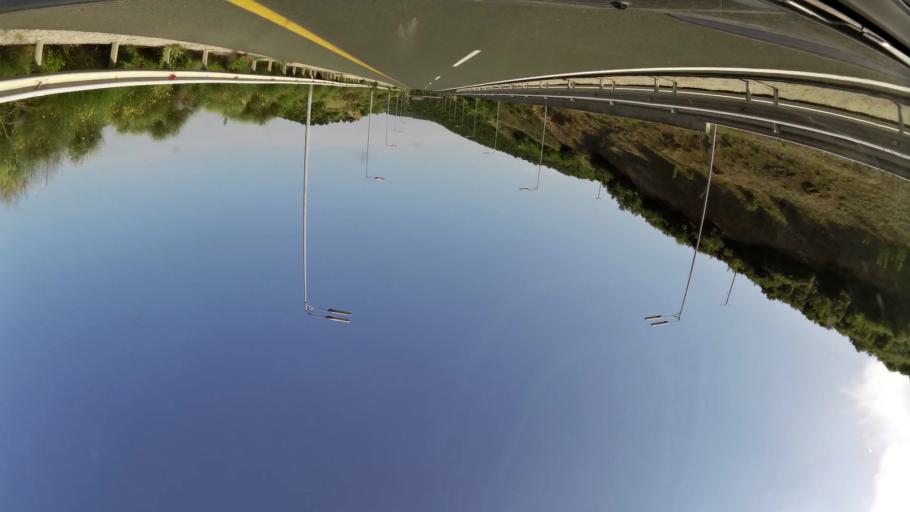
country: GR
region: Central Macedonia
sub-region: Nomos Imathias
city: Veroia
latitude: 40.4428
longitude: 22.1983
